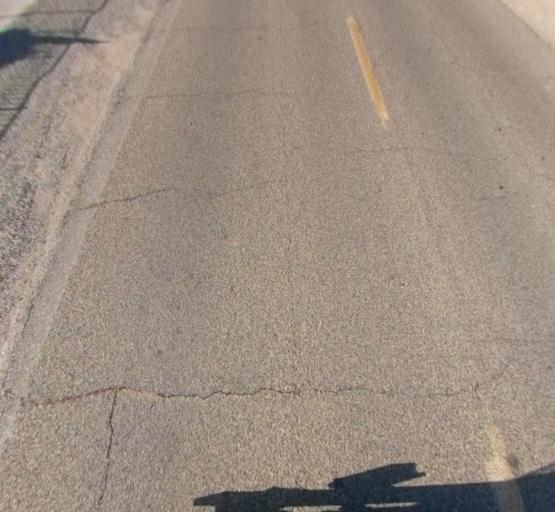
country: US
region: California
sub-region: Madera County
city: Madera
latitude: 36.9504
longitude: -120.1103
